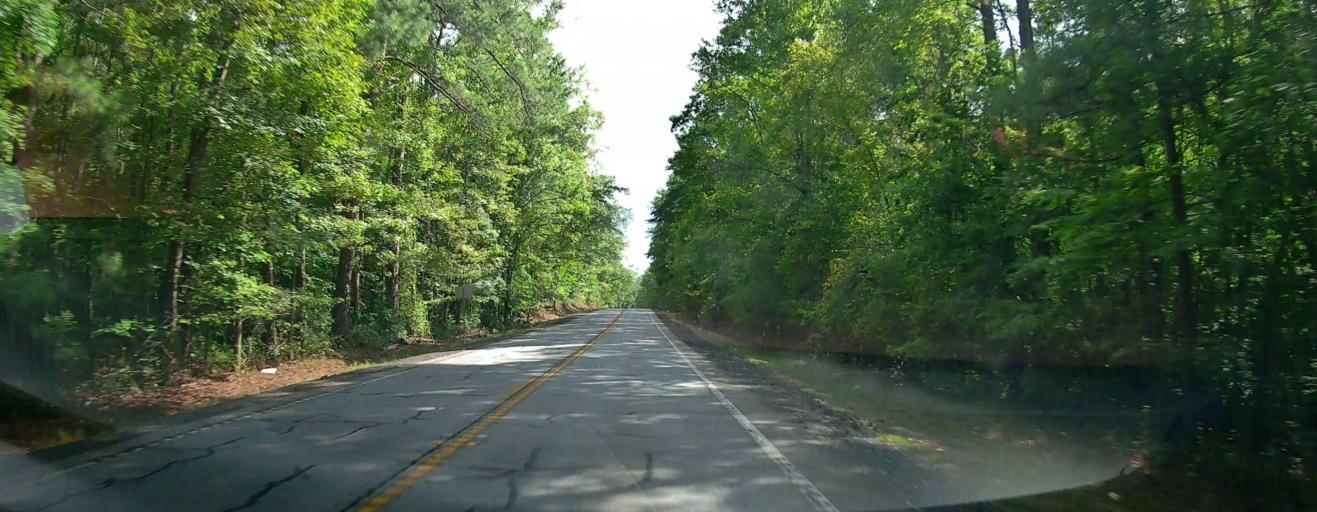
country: US
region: Georgia
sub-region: Harris County
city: Hamilton
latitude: 32.7910
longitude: -84.8705
